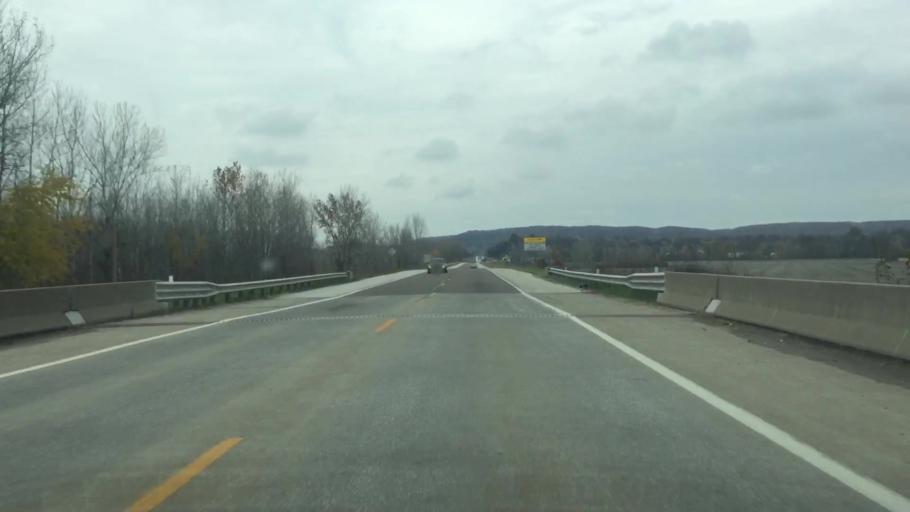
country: US
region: Missouri
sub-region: Gasconade County
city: Hermann
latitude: 38.7200
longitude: -91.4429
